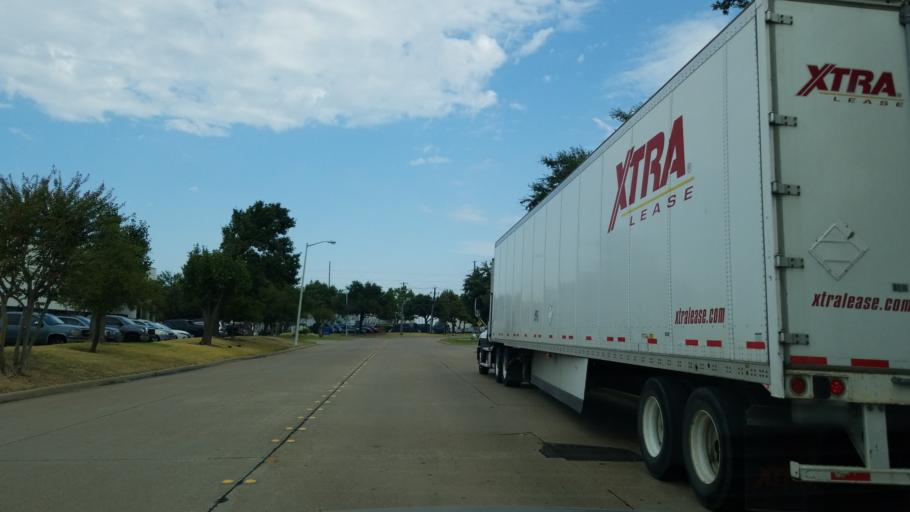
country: US
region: Texas
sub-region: Dallas County
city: Garland
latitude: 32.9053
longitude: -96.6741
